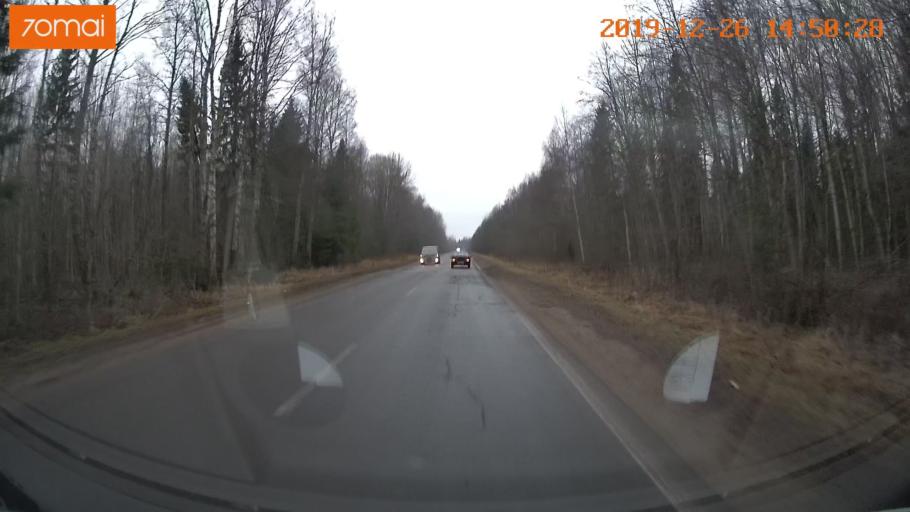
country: RU
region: Jaroslavl
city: Poshekhon'ye
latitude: 58.3317
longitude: 38.9250
